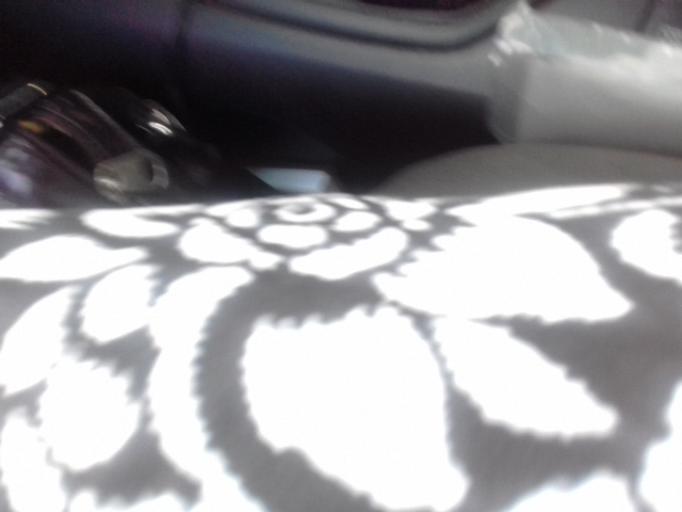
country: LS
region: Thaba-Tseka
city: Thaba-Tseka
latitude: -29.5255
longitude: 28.3447
